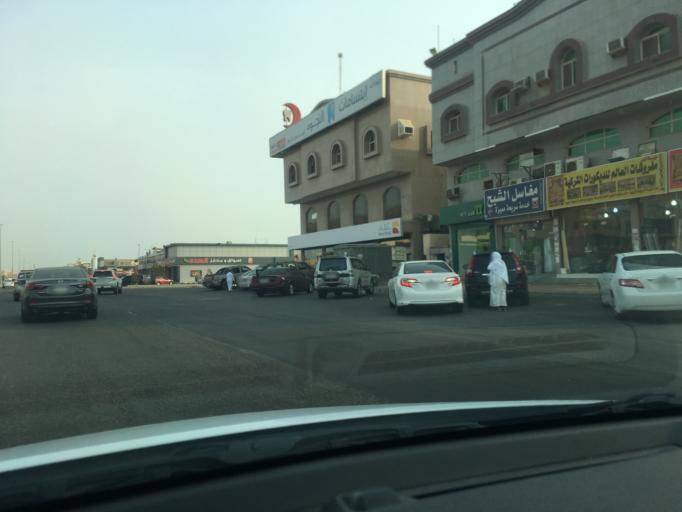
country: SA
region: Makkah
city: Jeddah
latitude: 21.7575
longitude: 39.1849
